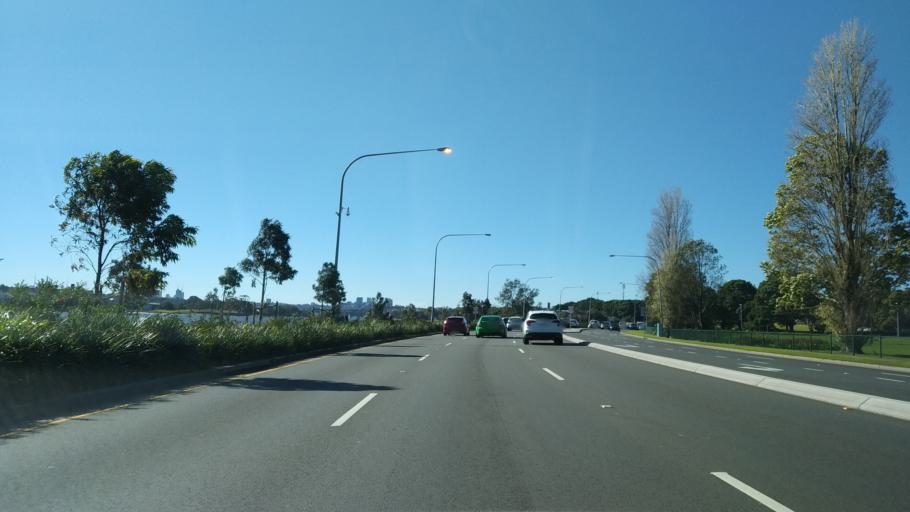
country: AU
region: New South Wales
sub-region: Leichhardt
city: Leichhardt
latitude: -33.8702
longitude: 151.1432
